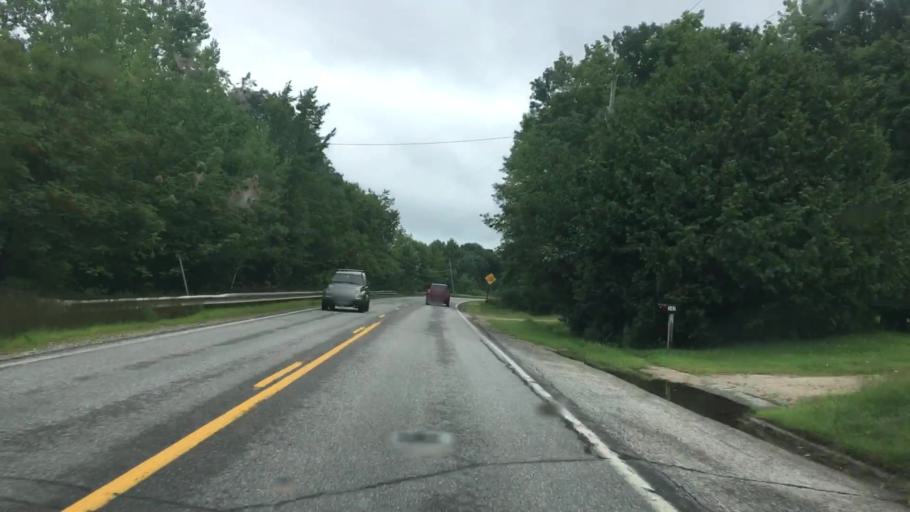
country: US
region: Maine
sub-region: Oxford County
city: Brownfield
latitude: 43.9614
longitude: -70.9030
